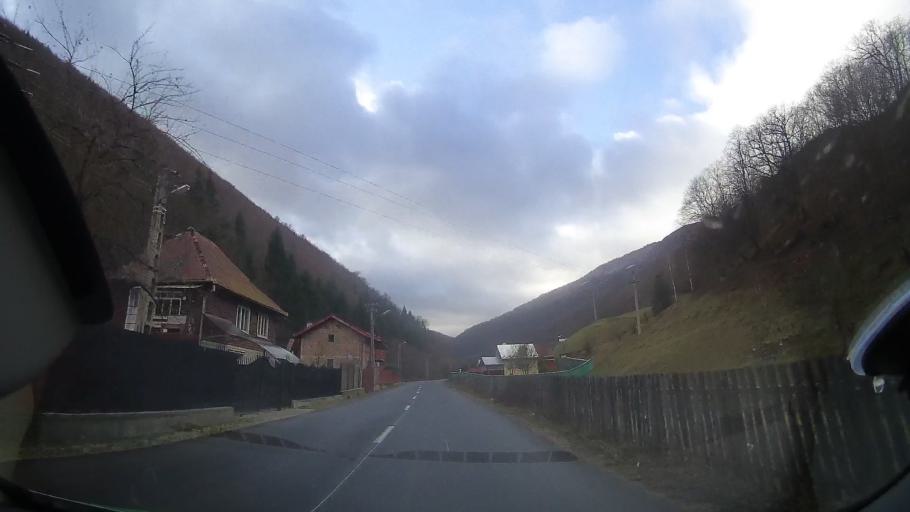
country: RO
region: Cluj
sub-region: Comuna Valea Ierii
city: Valea Ierii
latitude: 46.6849
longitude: 23.2726
